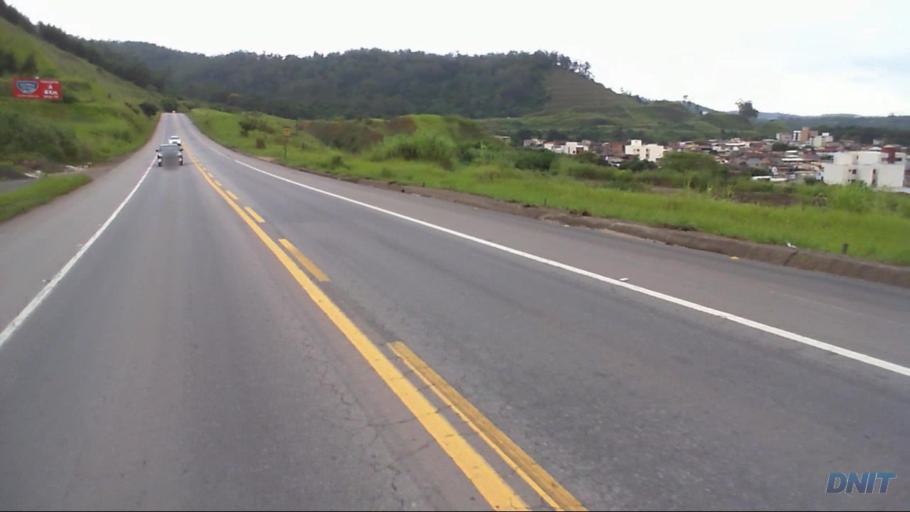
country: BR
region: Minas Gerais
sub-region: Coronel Fabriciano
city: Coronel Fabriciano
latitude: -19.5271
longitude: -42.5800
